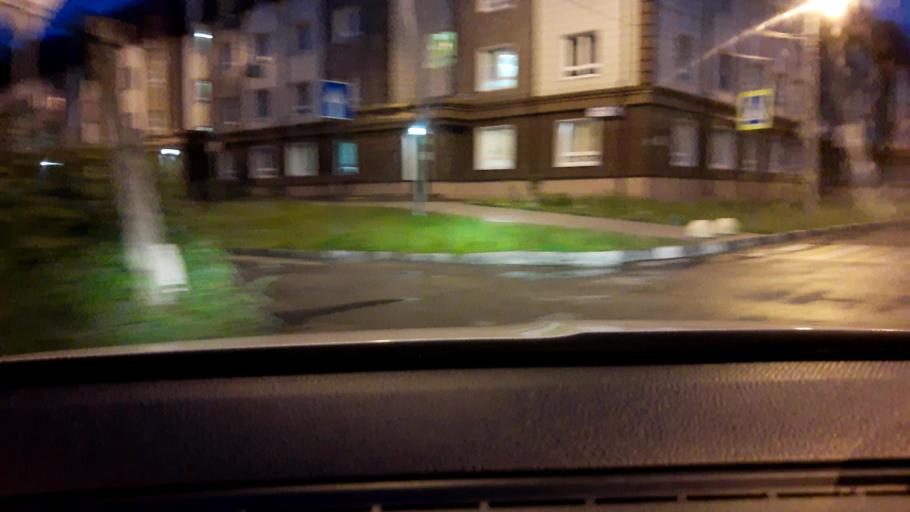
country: RU
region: Moskovskaya
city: Lesnyye Polyany
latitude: 55.9206
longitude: 37.8837
